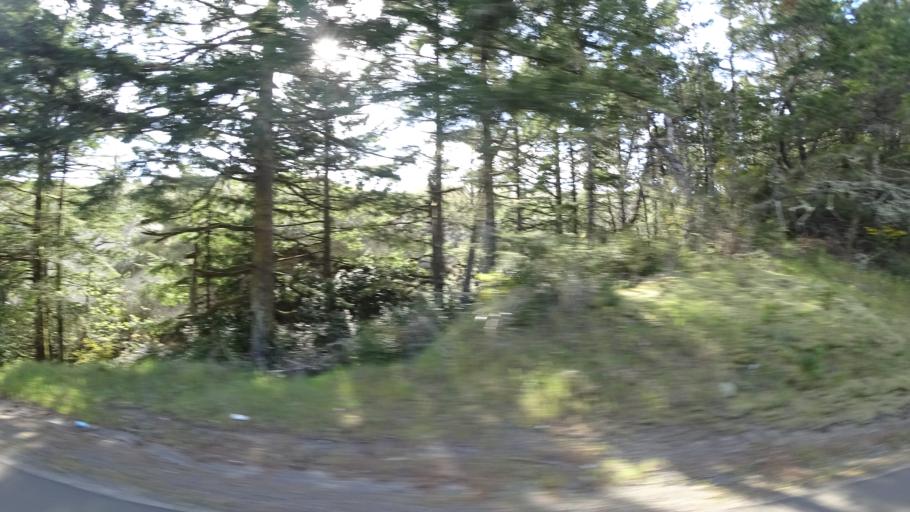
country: US
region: Oregon
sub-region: Lane County
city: Dunes City
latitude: 43.8928
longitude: -124.1188
